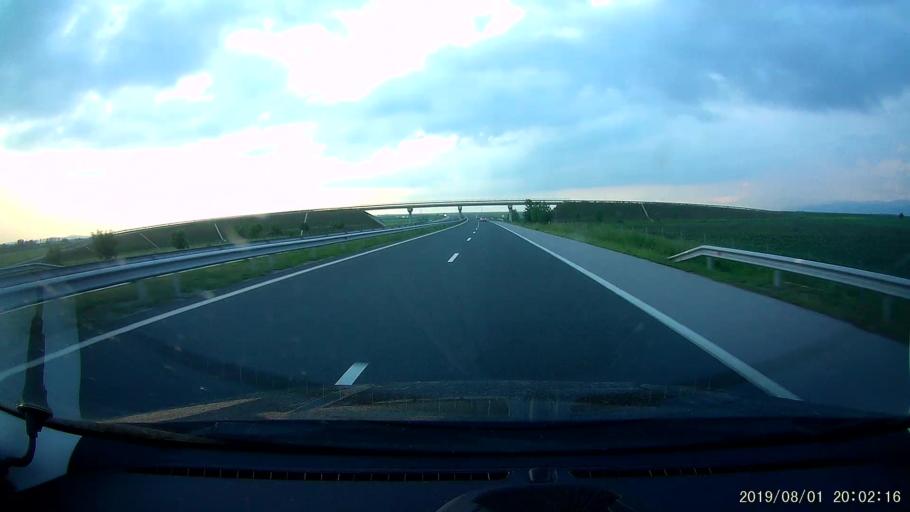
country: BG
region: Yambol
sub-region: Obshtina Straldzha
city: Straldzha
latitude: 42.5592
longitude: 26.6352
